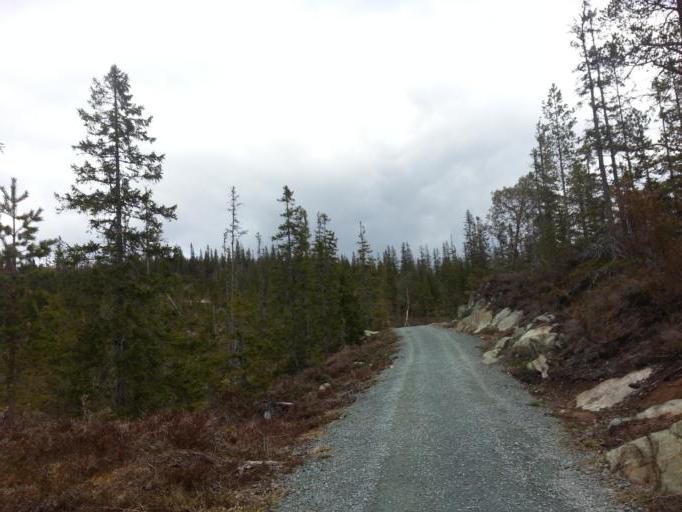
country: NO
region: Nord-Trondelag
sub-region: Levanger
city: Skogn
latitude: 63.5863
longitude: 11.0883
